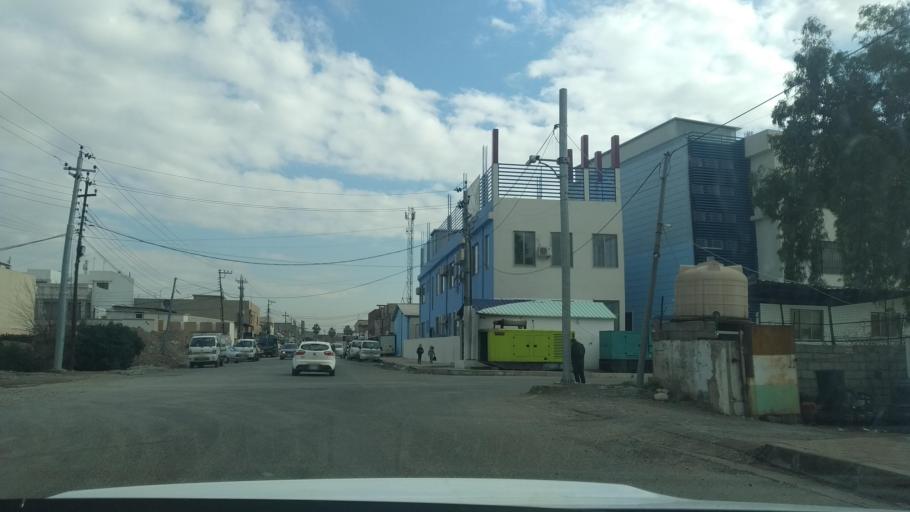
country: IQ
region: Arbil
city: Erbil
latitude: 36.1852
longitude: 43.9898
